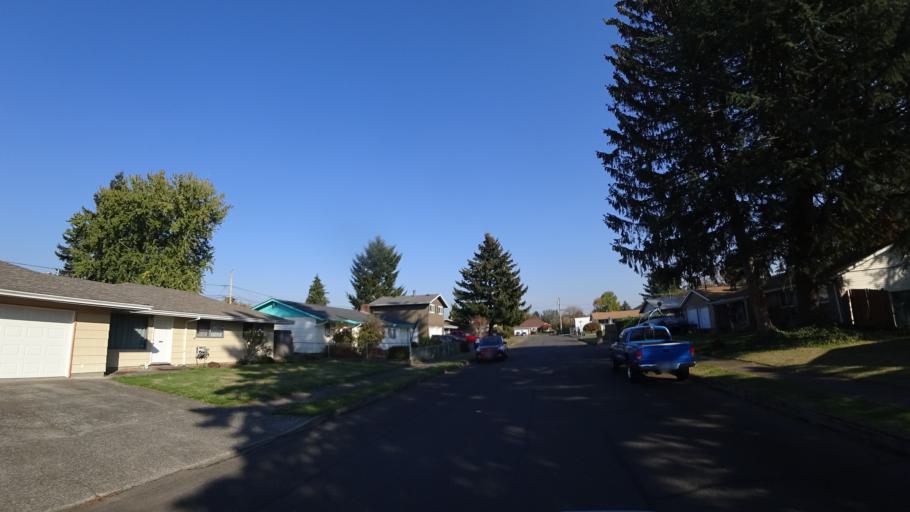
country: US
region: Oregon
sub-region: Multnomah County
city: Gresham
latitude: 45.5164
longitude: -122.4315
